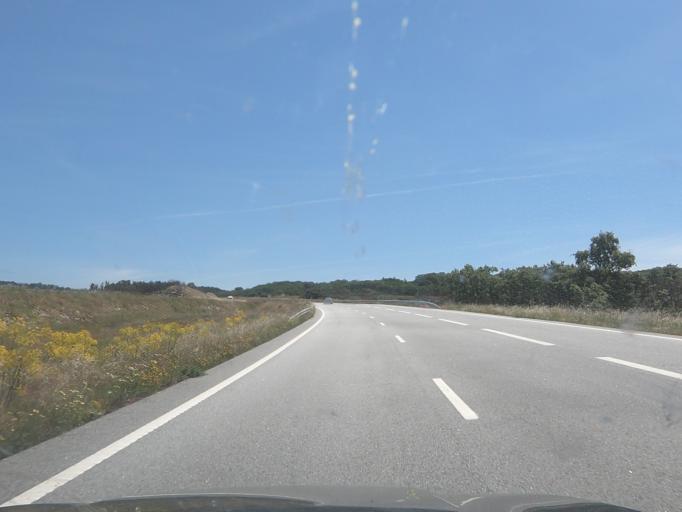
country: PT
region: Guarda
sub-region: Pinhel
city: Pinhel
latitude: 40.6040
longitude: -7.0277
